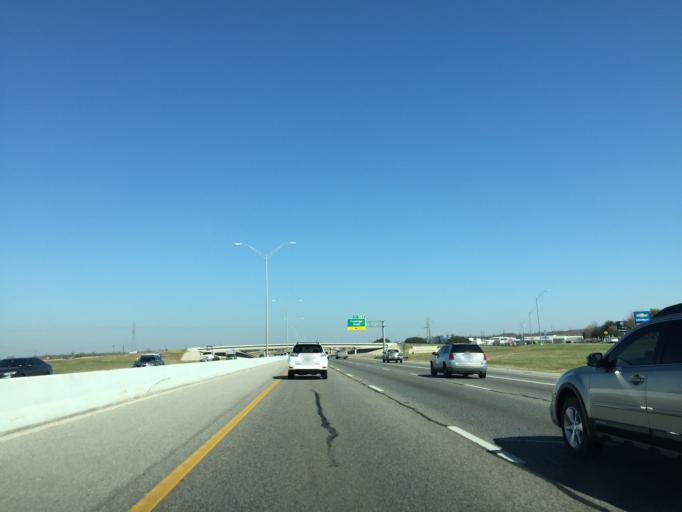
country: US
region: Texas
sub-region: Williamson County
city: Georgetown
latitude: 30.5740
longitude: -97.6928
